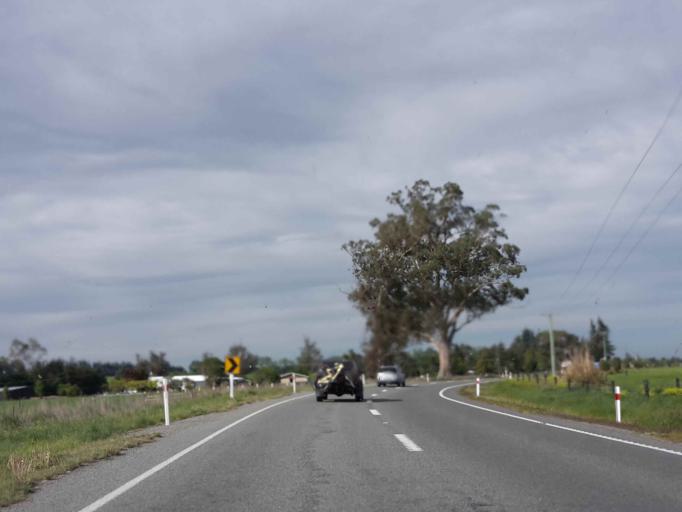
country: NZ
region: Canterbury
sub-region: Timaru District
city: Pleasant Point
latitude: -44.1137
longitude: 171.2152
